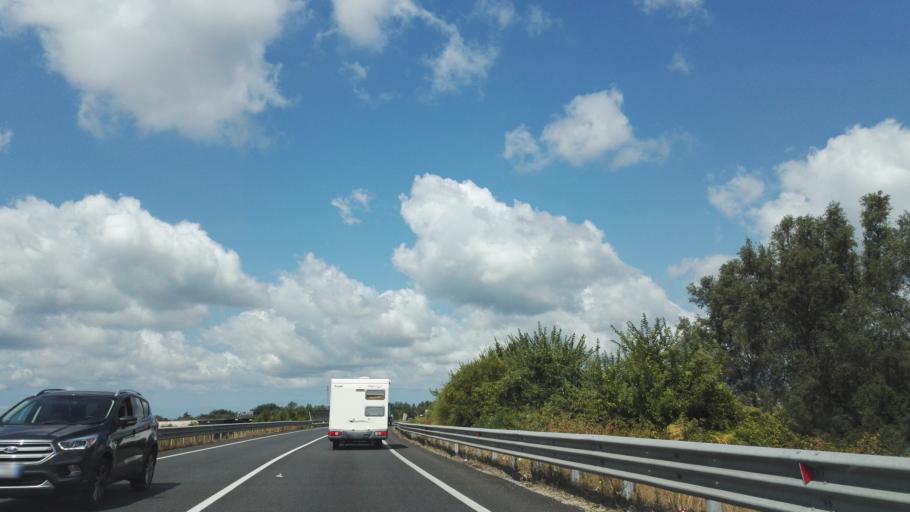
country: IT
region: Calabria
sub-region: Provincia di Reggio Calabria
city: Cinque Frondi
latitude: 38.4177
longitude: 16.0721
